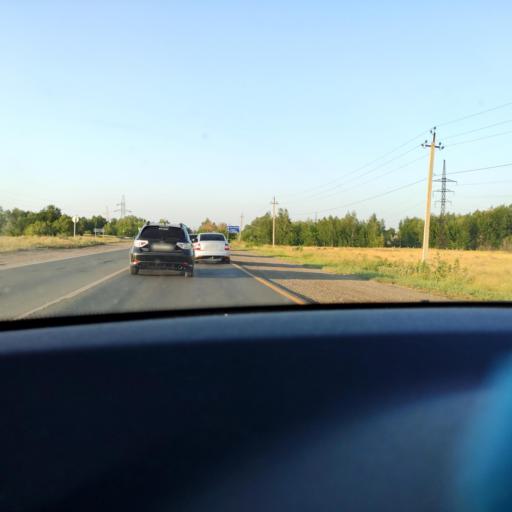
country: RU
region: Samara
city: Kinel'
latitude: 53.2473
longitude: 50.5889
